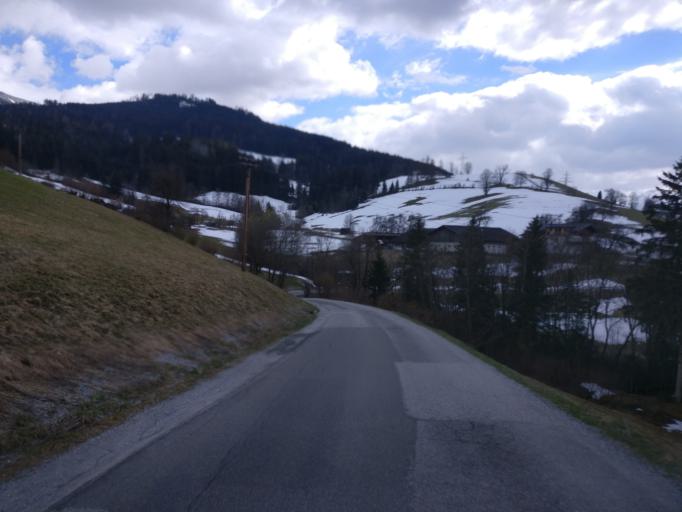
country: AT
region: Salzburg
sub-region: Politischer Bezirk Sankt Johann im Pongau
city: Bischofshofen
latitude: 47.4222
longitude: 13.2342
